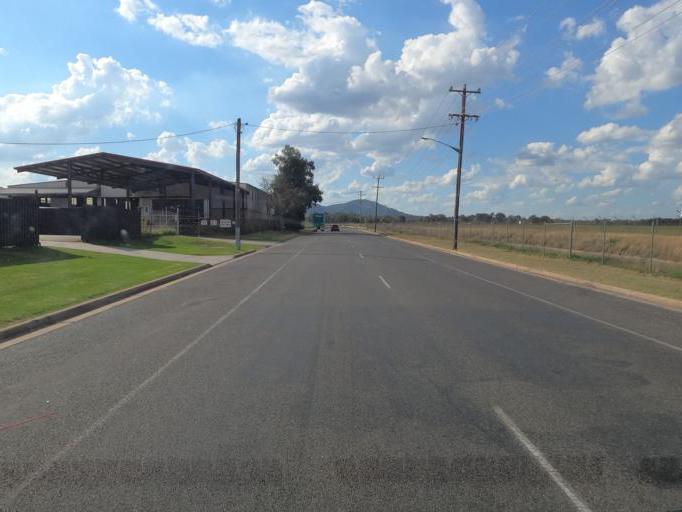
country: AU
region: New South Wales
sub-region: Albury Municipality
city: East Albury
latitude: -36.0725
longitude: 146.9481
